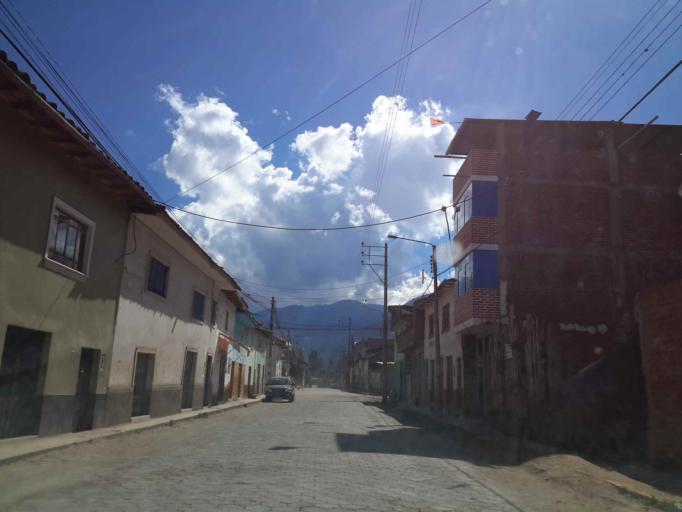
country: PE
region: Apurimac
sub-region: Provincia de Andahuaylas
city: Talavera
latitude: -13.6518
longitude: -73.4331
